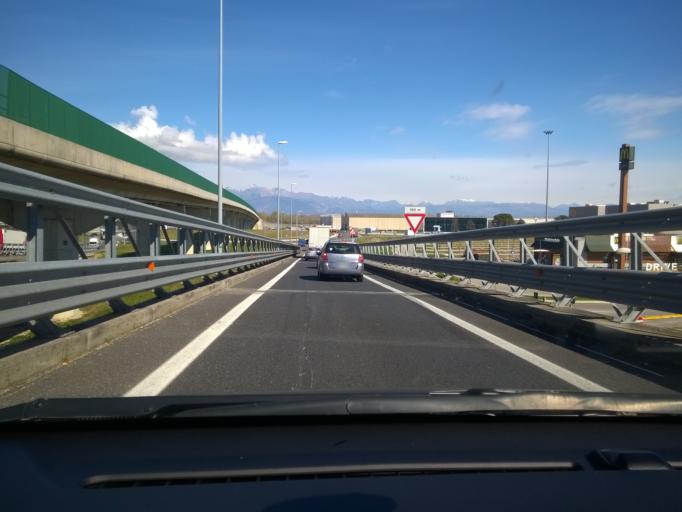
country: IT
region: Friuli Venezia Giulia
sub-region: Provincia di Pordenone
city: Fiume Veneto
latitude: 45.9441
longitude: 12.7209
